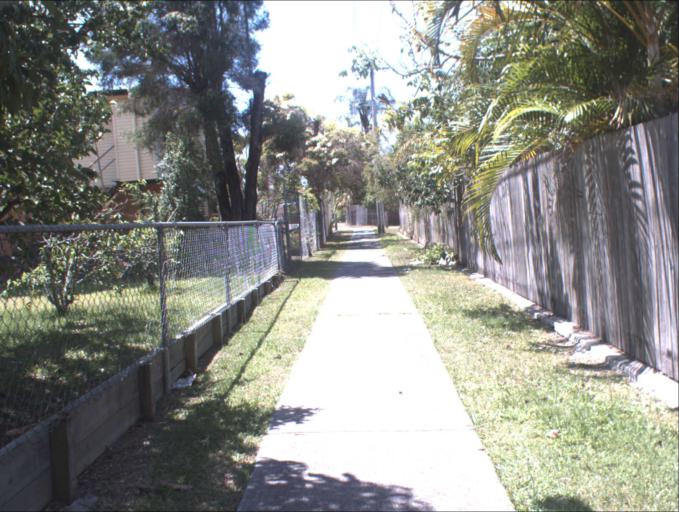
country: AU
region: Queensland
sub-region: Logan
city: Logan City
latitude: -27.6539
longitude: 153.1068
